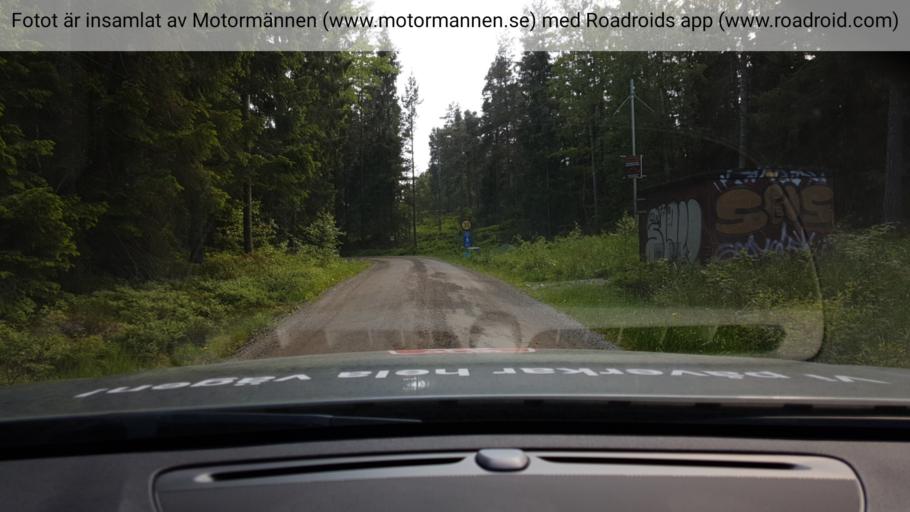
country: SE
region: Stockholm
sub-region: Varmdo Kommun
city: Mortnas
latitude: 59.2493
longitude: 18.4577
